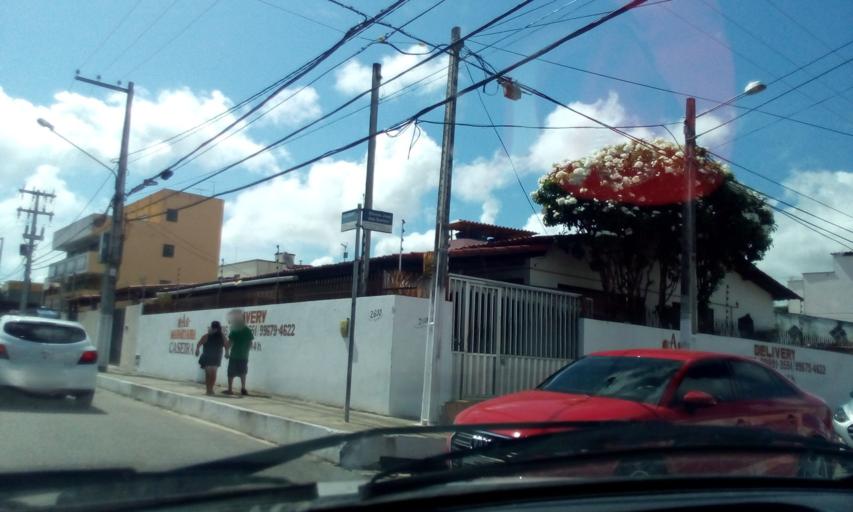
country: BR
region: Rio Grande do Norte
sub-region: Parnamirim
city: Parnamirim
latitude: -5.8846
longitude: -35.2011
